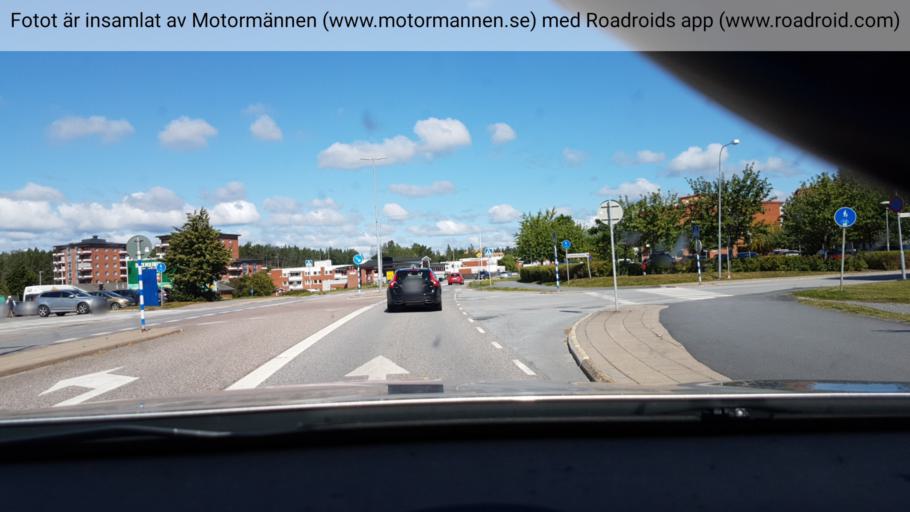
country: SE
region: Stockholm
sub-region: Norrtalje Kommun
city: Norrtalje
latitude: 59.7604
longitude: 18.6909
